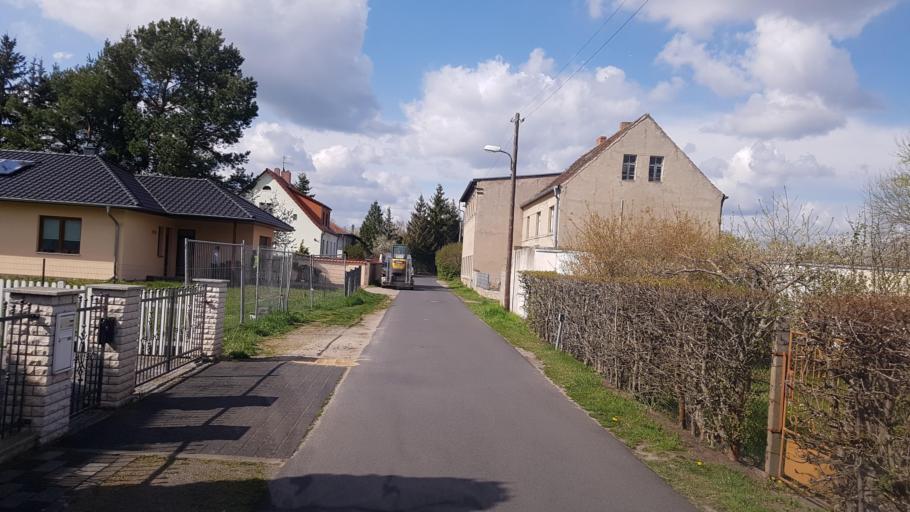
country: DE
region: Brandenburg
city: Luckenwalde
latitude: 52.0766
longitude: 13.1443
